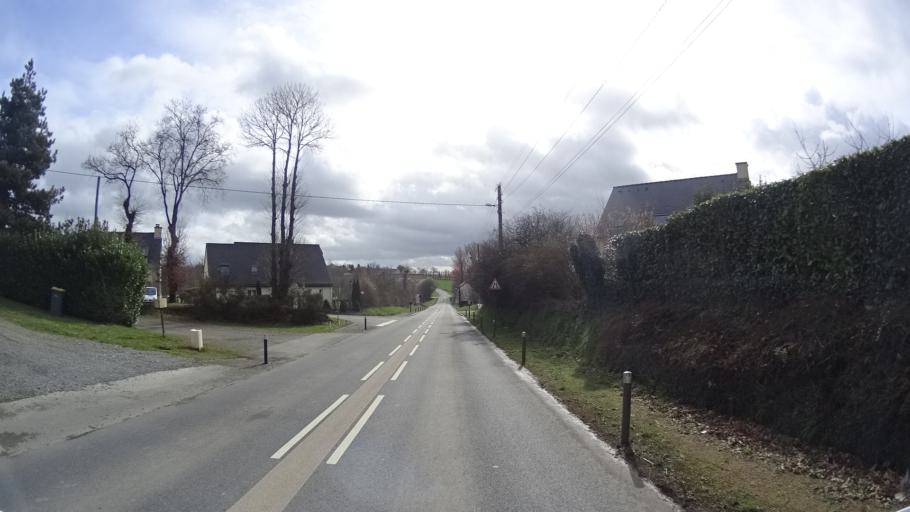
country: FR
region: Brittany
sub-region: Departement d'Ille-et-Vilaine
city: Romille
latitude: 48.2109
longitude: -1.8896
